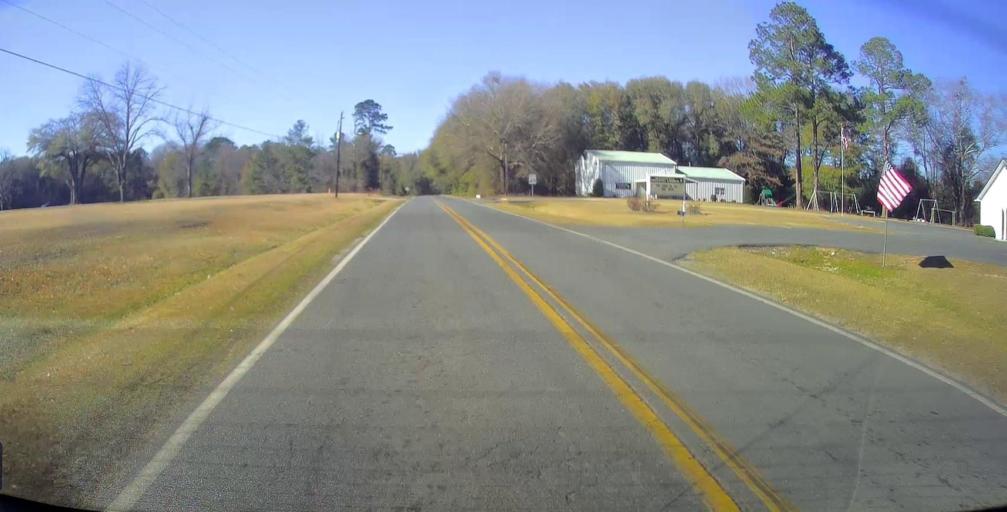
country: US
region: Georgia
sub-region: Macon County
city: Oglethorpe
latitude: 32.2966
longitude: -84.0554
